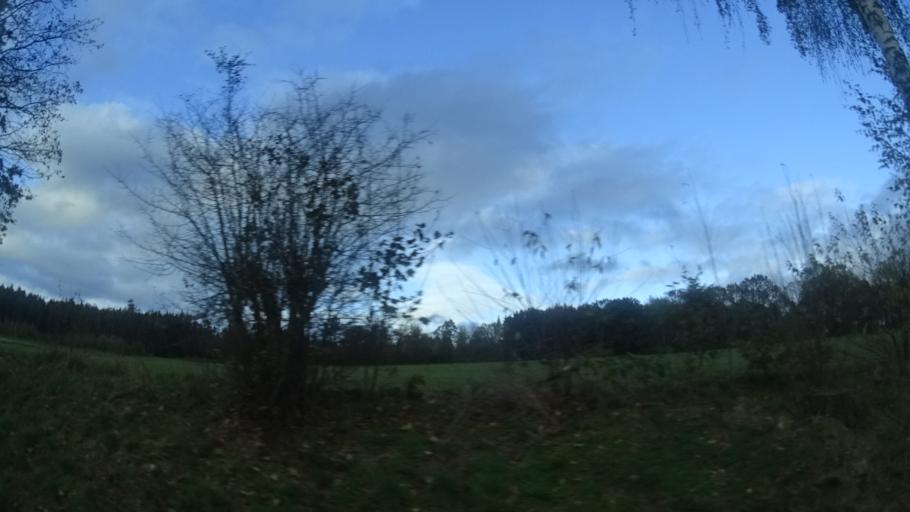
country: DE
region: Hesse
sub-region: Regierungsbezirk Kassel
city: Flieden
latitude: 50.4555
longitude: 9.5536
